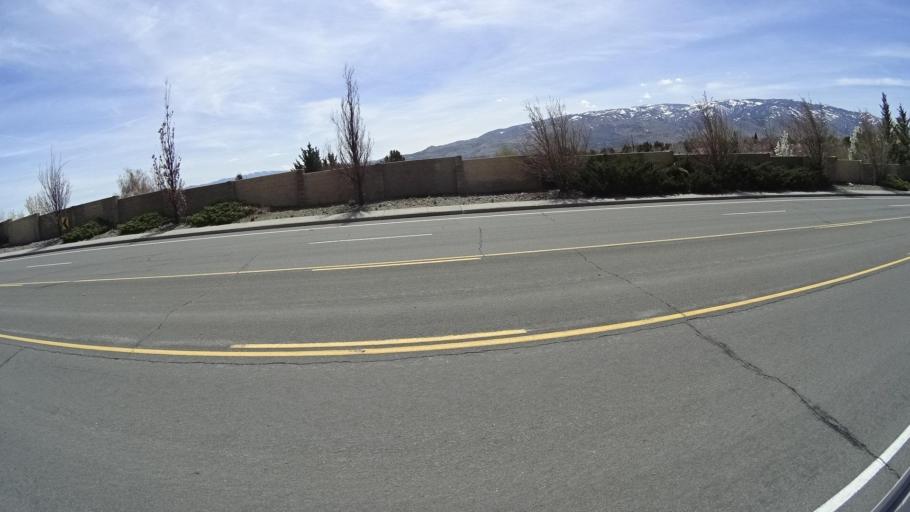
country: US
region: Nevada
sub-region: Washoe County
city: Mogul
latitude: 39.5353
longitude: -119.8772
